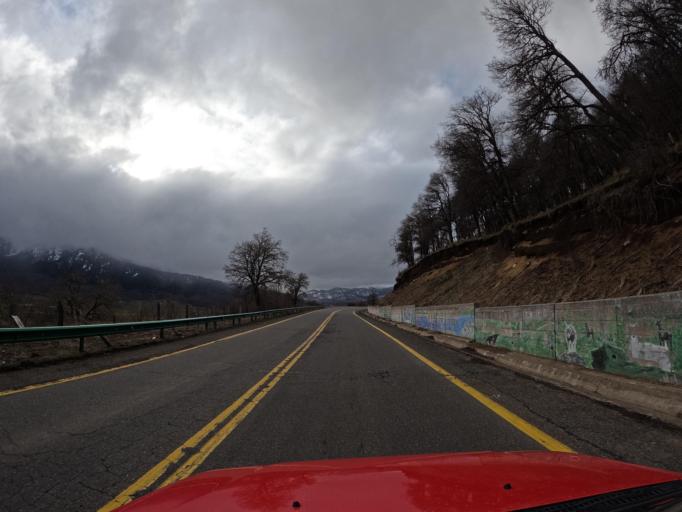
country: AR
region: Neuquen
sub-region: Departamento de Loncopue
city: Loncopue
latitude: -38.4762
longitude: -71.3631
